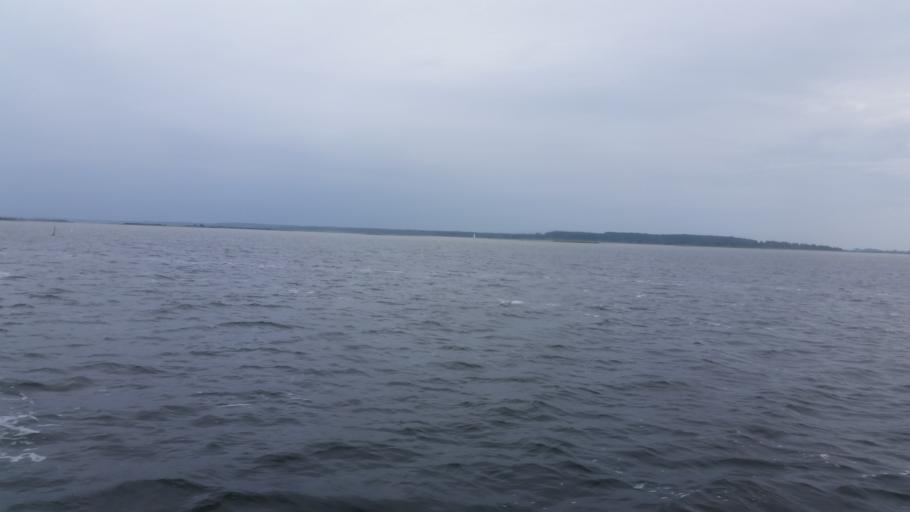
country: DE
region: Mecklenburg-Vorpommern
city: Hiddensee
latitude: 54.5677
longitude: 13.1314
